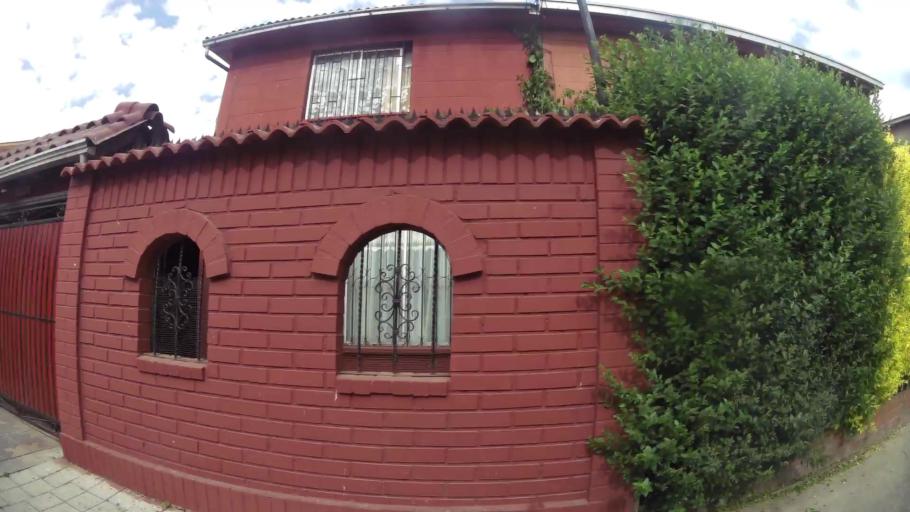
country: CL
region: Santiago Metropolitan
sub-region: Provincia de Cordillera
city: Puente Alto
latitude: -33.6213
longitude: -70.6165
